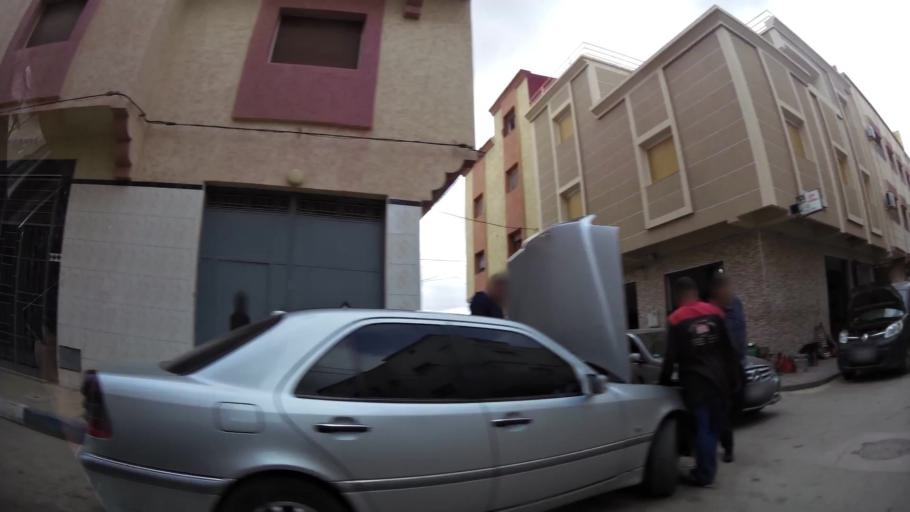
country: MA
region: Oriental
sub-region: Nador
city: Nador
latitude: 35.1633
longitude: -2.9130
